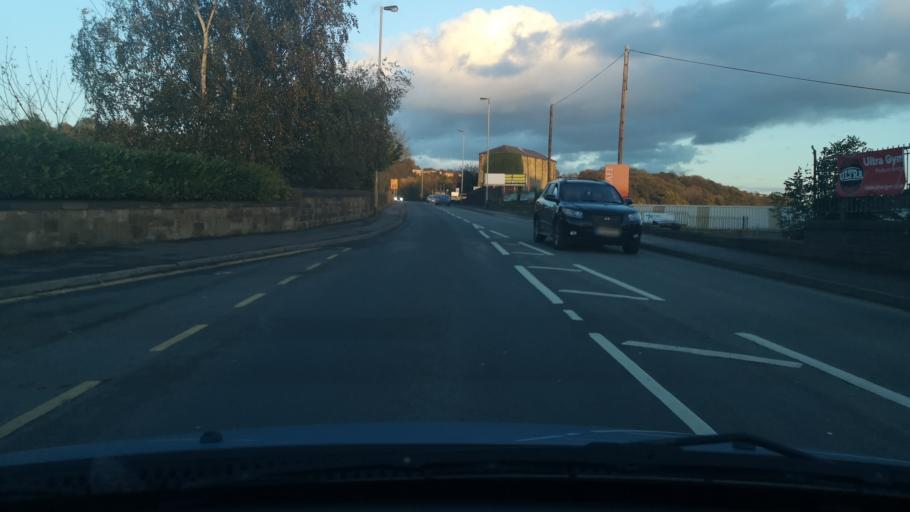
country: GB
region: England
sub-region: City and Borough of Wakefield
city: Horbury
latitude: 53.6584
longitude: -1.5713
